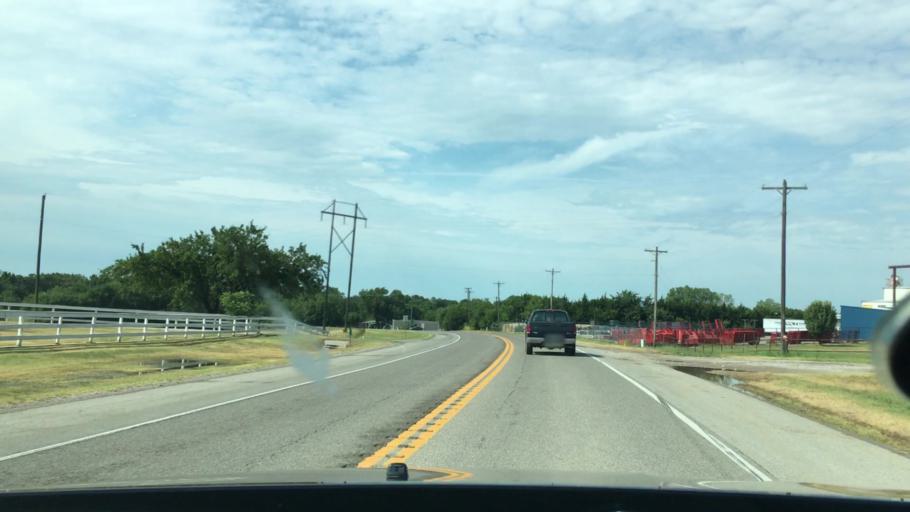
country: US
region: Oklahoma
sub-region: Murray County
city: Sulphur
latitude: 34.5288
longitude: -96.9690
